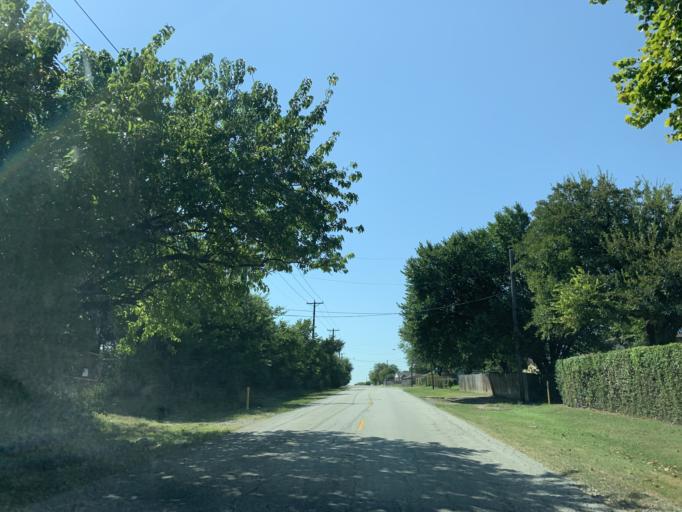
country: US
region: Texas
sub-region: Dallas County
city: Hutchins
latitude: 32.6709
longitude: -96.7456
